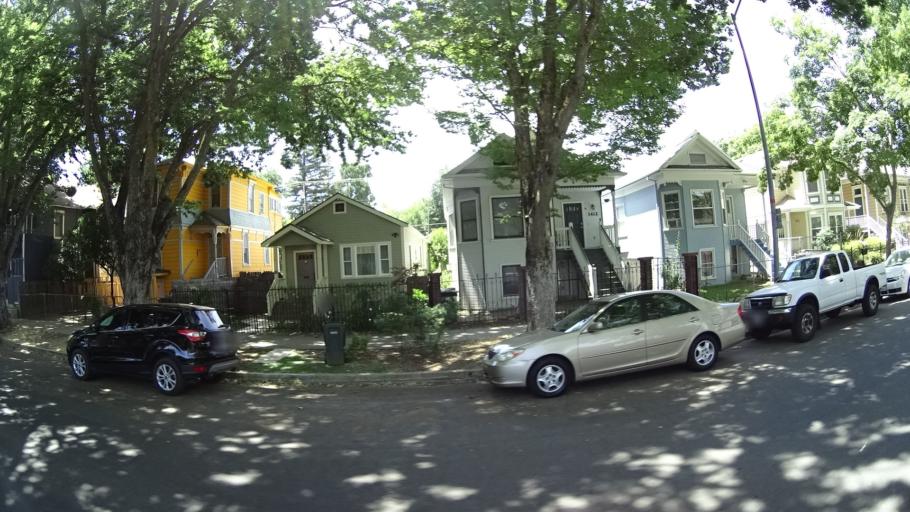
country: US
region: California
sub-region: Sacramento County
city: Sacramento
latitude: 38.5852
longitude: -121.4843
